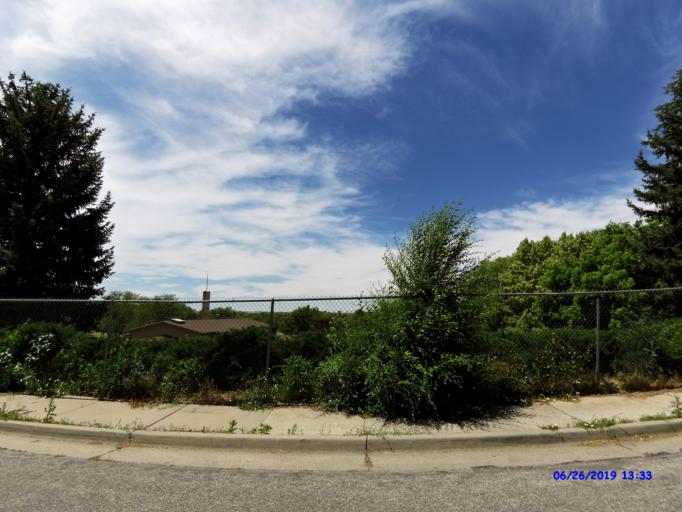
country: US
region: Utah
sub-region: Weber County
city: South Ogden
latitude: 41.2047
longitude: -111.9626
